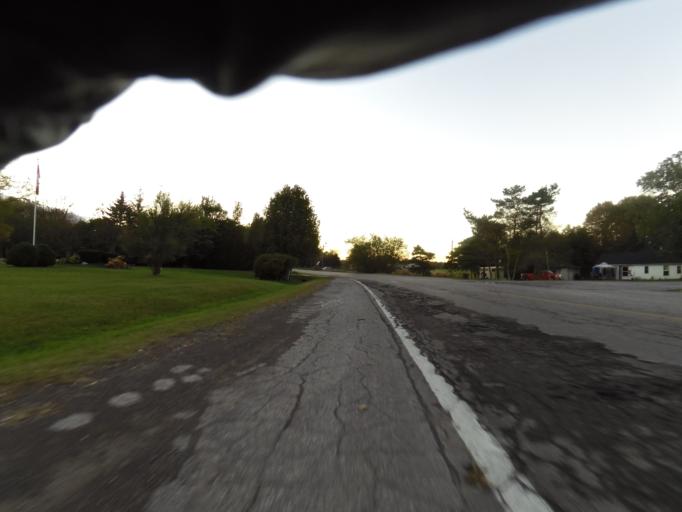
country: CA
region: Ontario
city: Quinte West
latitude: 44.0390
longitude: -77.6598
